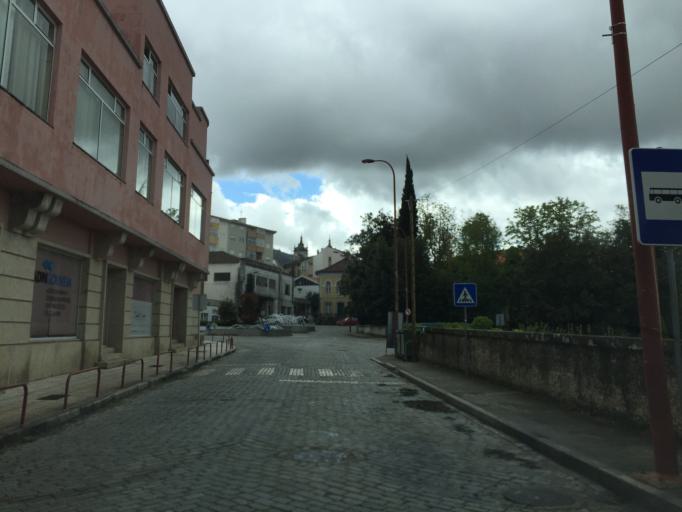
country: PT
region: Guarda
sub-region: Manteigas
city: Manteigas
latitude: 40.4963
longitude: -7.5927
